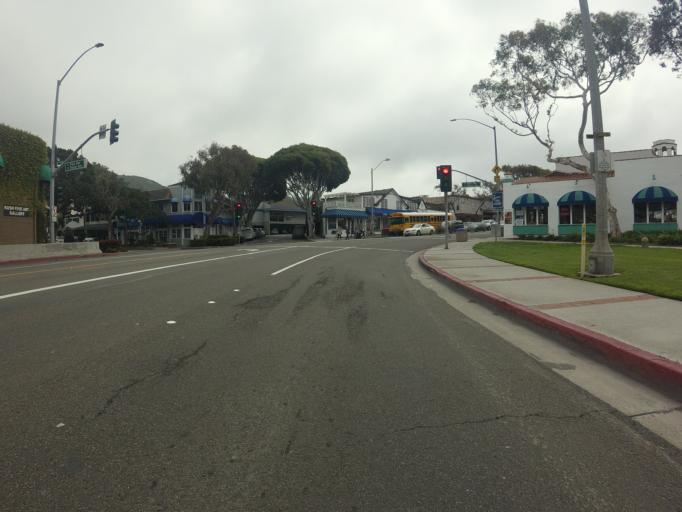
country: US
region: California
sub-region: Orange County
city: Laguna Beach
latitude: 33.5421
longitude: -117.7837
